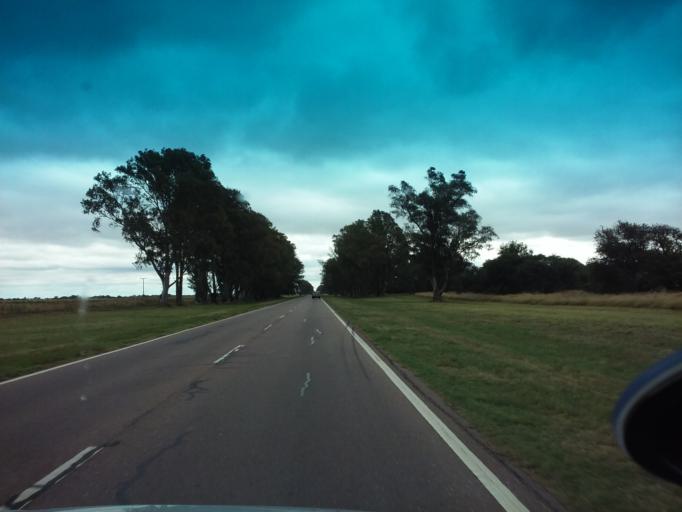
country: AR
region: La Pampa
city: Santa Rosa
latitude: -36.5725
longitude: -64.1510
